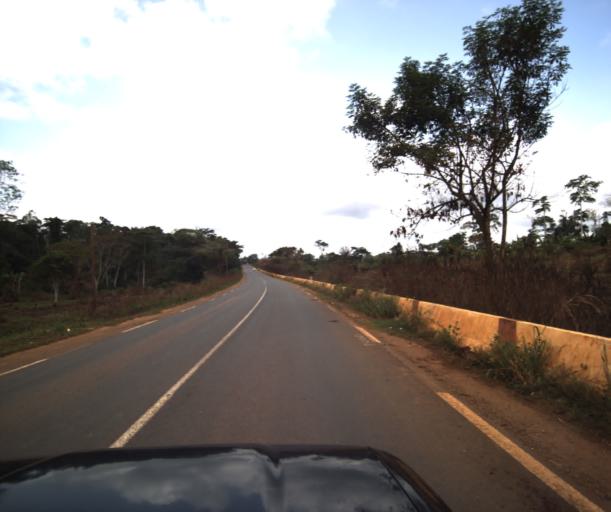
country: CM
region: Centre
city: Mbankomo
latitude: 3.7915
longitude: 11.4165
